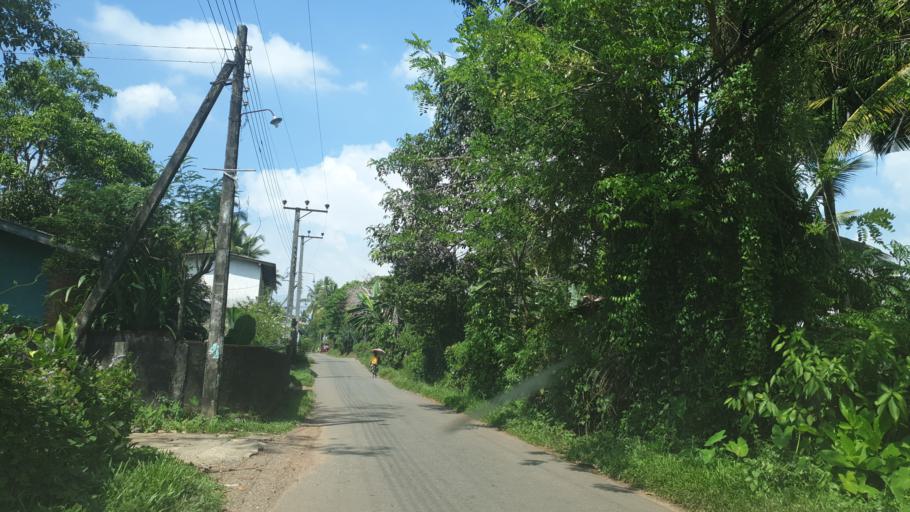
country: LK
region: Western
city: Horana South
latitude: 6.7070
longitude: 79.9838
